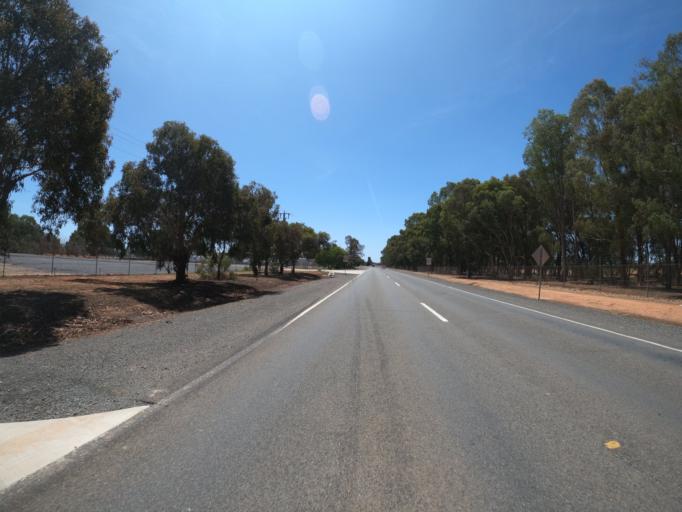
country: AU
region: Victoria
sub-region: Moira
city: Yarrawonga
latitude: -36.0352
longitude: 145.9955
